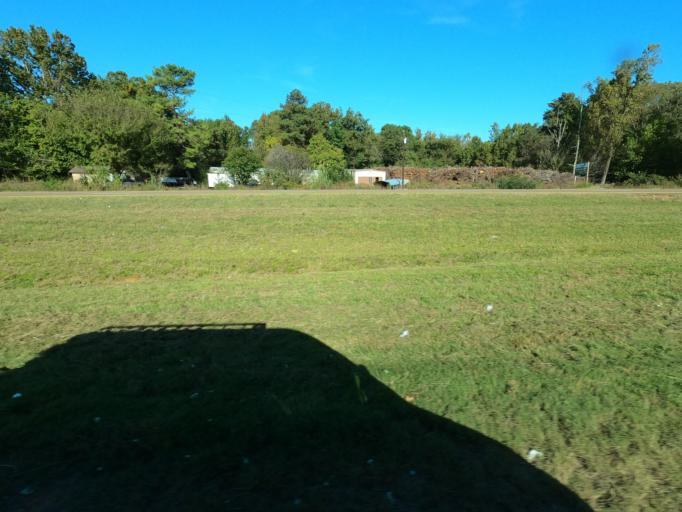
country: US
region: Tennessee
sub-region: Tipton County
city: Munford
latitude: 35.4272
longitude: -89.8112
